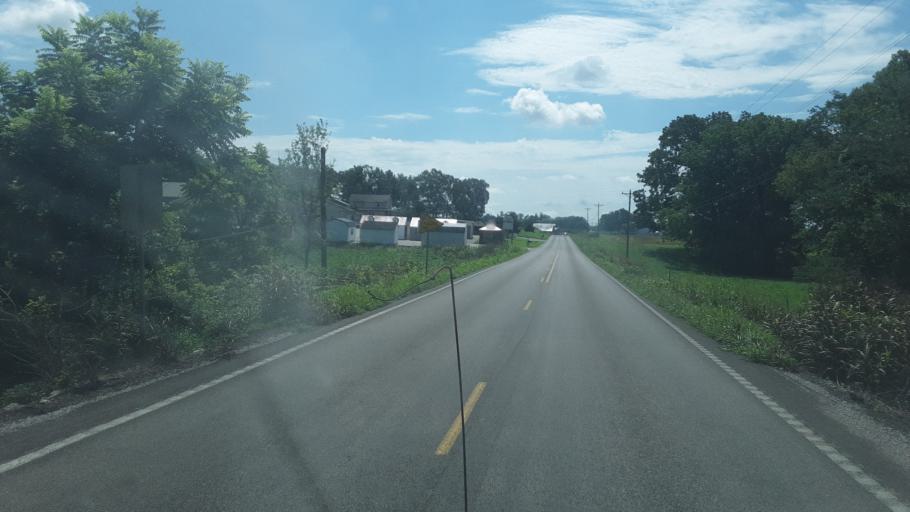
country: US
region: Kentucky
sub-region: Christian County
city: Oak Grove
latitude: 36.7674
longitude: -87.3329
